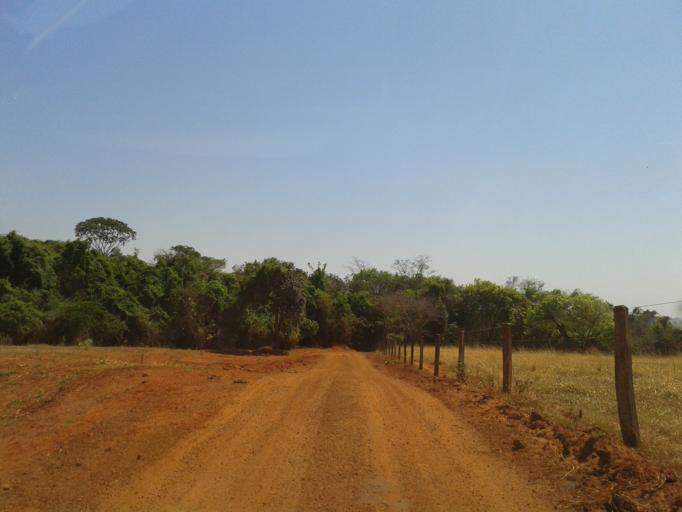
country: BR
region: Minas Gerais
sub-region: Ituiutaba
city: Ituiutaba
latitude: -19.0516
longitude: -49.3779
